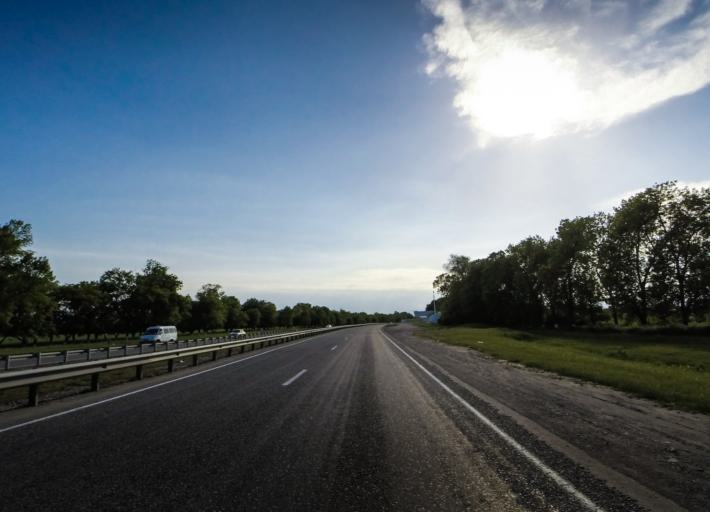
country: RU
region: Kabardino-Balkariya
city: Nartan
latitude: 43.4885
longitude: 43.6799
